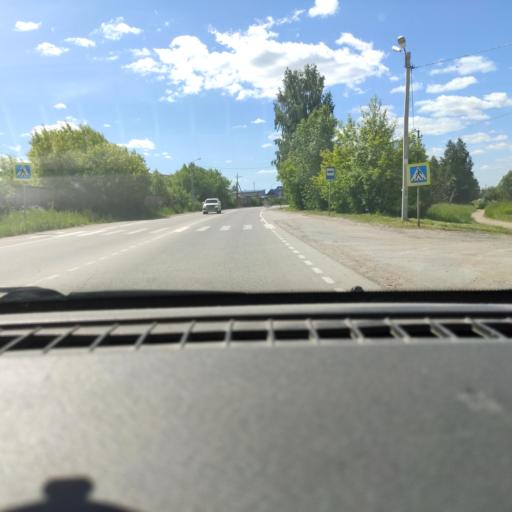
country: RU
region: Perm
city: Krasnokamsk
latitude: 58.0774
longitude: 55.6996
